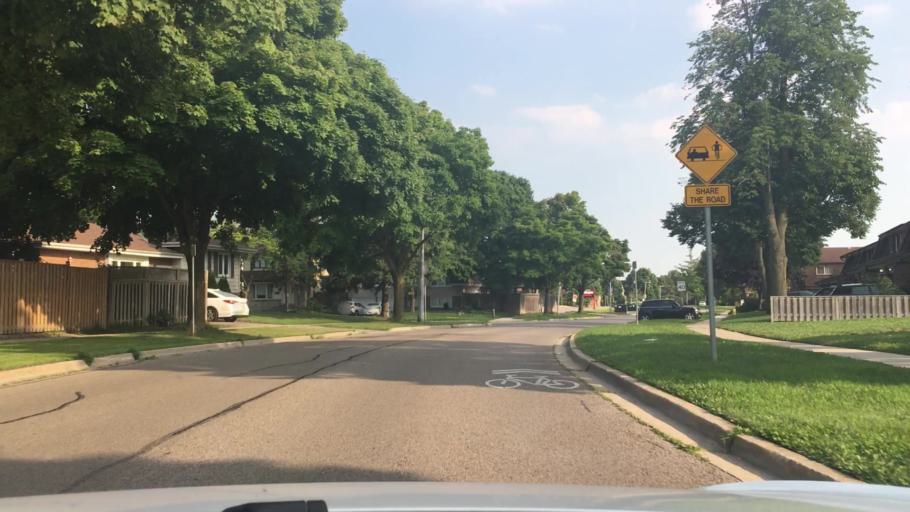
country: CA
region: Ontario
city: Ajax
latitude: 43.8738
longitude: -78.9539
